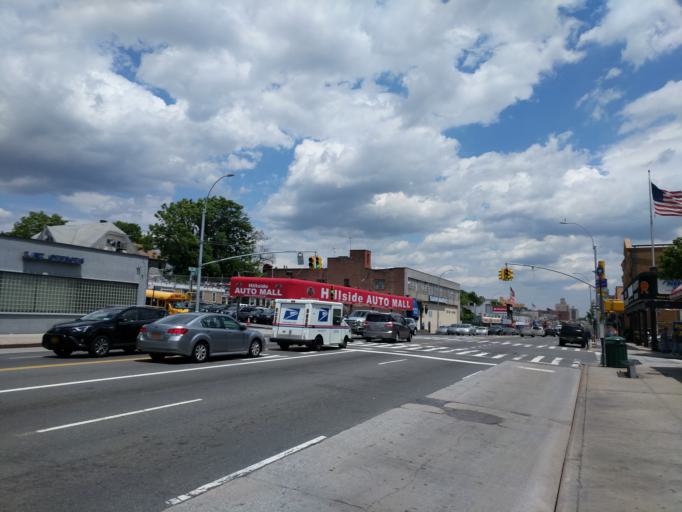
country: US
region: New York
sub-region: Queens County
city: Jamaica
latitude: 40.7064
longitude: -73.8069
